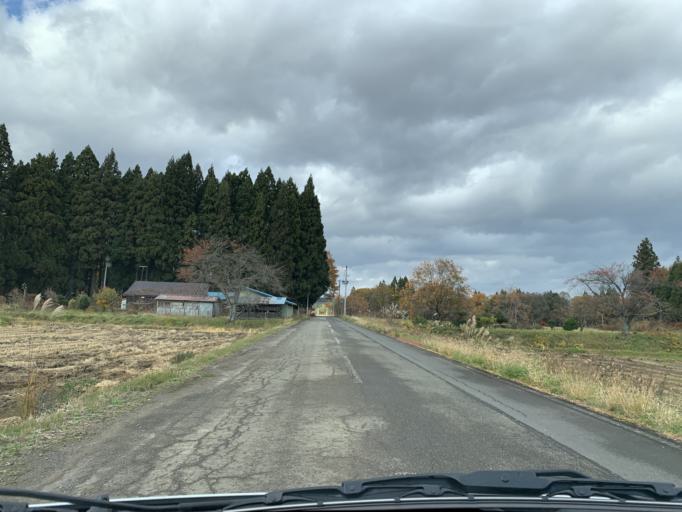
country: JP
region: Iwate
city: Mizusawa
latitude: 39.1137
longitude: 140.9736
